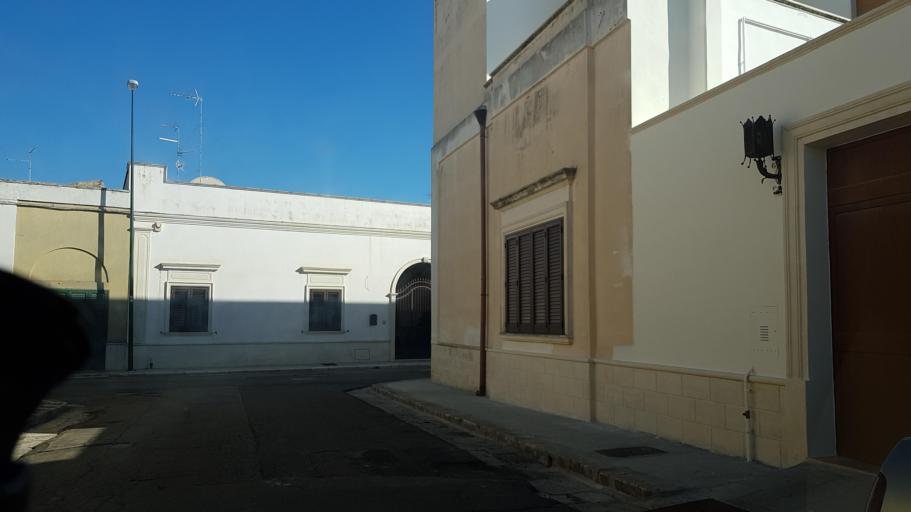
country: IT
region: Apulia
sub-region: Provincia di Lecce
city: Campi Salentina
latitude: 40.3965
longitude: 18.0233
